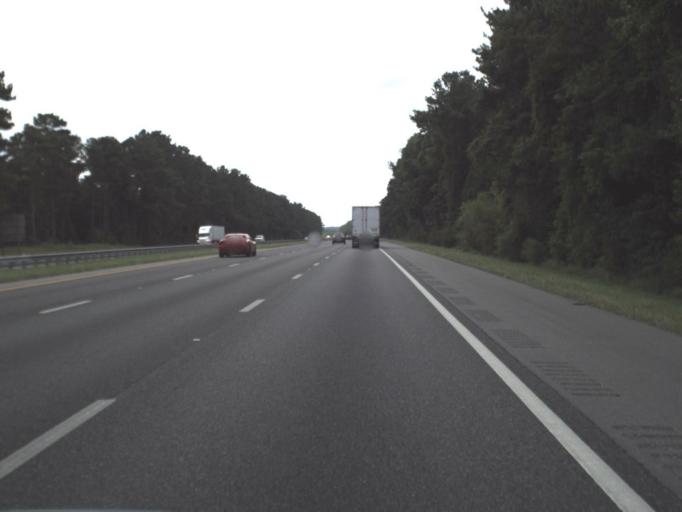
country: US
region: Florida
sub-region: Alachua County
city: High Springs
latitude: 29.9501
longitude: -82.5683
